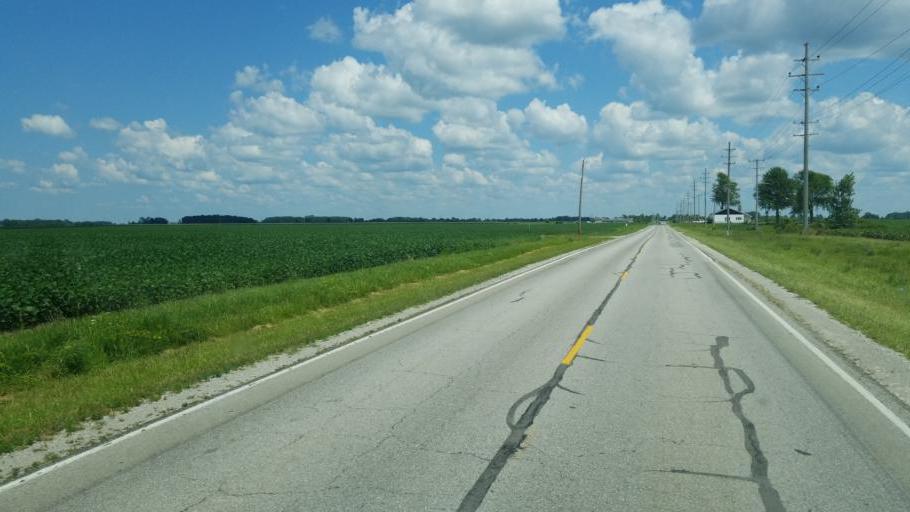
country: US
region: Ohio
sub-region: Marion County
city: Marion
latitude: 40.6303
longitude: -83.0604
